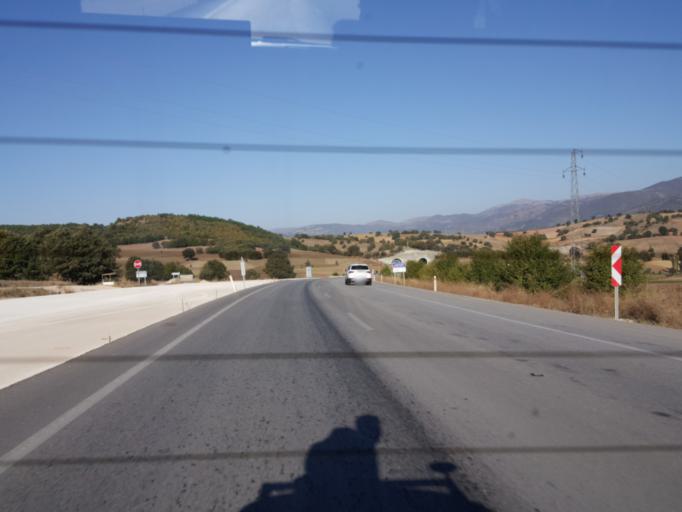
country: TR
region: Amasya
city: Ezinepazari
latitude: 40.5517
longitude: 36.1441
